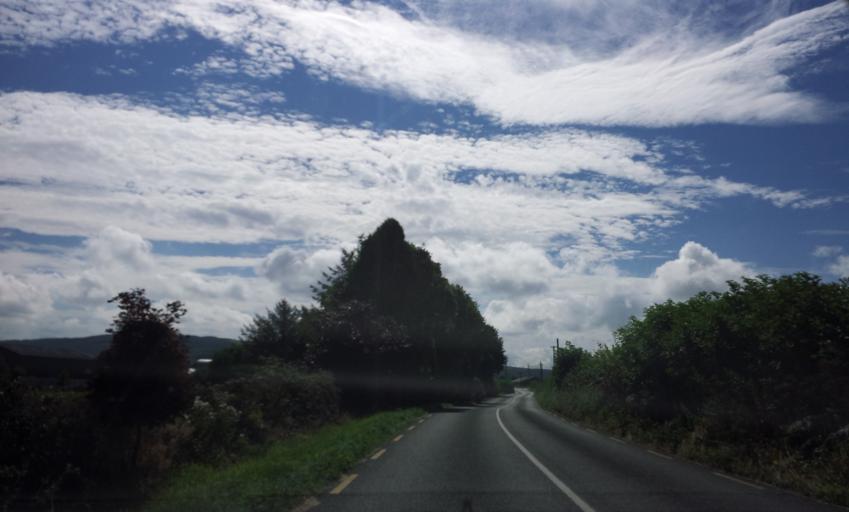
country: IE
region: Leinster
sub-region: Laois
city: Stradbally
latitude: 52.9734
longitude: -7.2133
